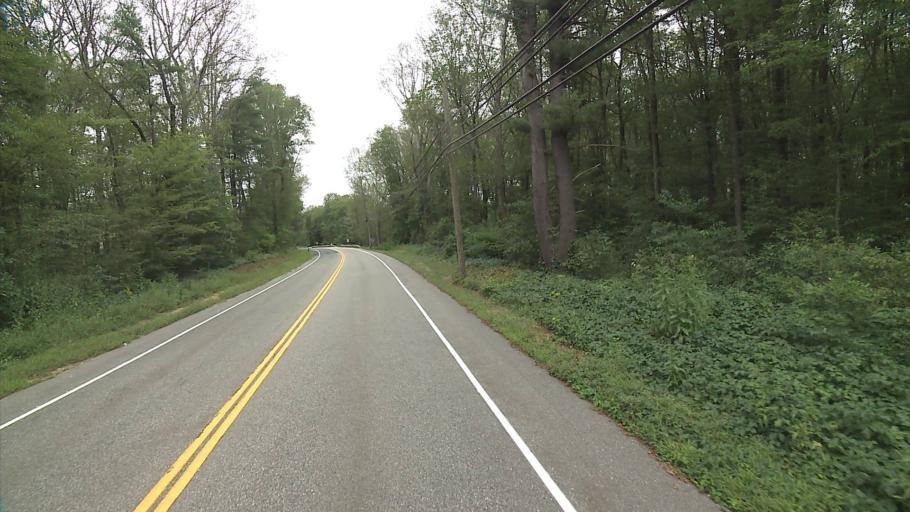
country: US
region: Connecticut
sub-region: Hartford County
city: Manchester
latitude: 41.7311
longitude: -72.4352
